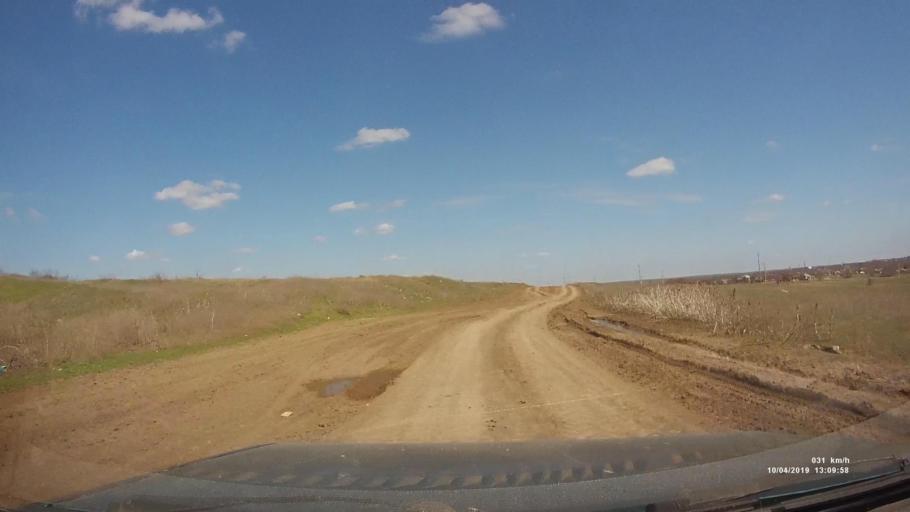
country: RU
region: Rostov
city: Masalovka
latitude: 48.4083
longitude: 40.2451
